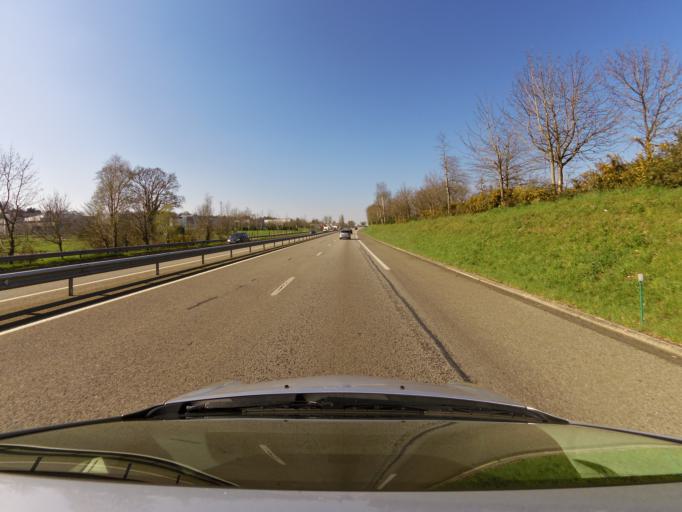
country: FR
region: Brittany
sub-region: Departement du Morbihan
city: Guer
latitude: 47.9353
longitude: -2.1179
